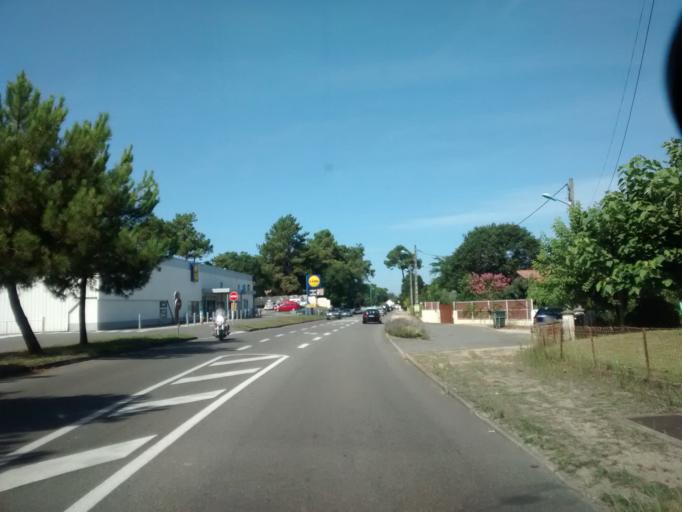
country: FR
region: Aquitaine
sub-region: Departement des Landes
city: Capbreton
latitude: 43.6363
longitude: -1.4190
